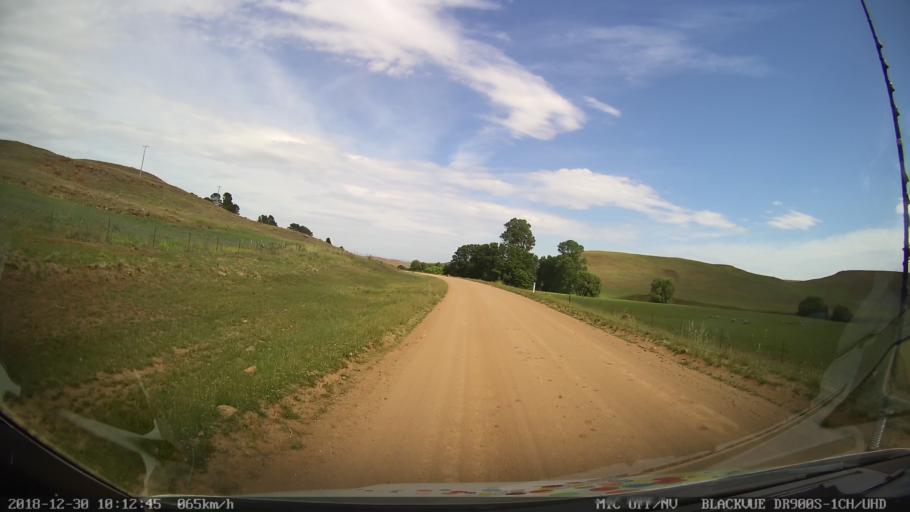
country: AU
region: New South Wales
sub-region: Snowy River
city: Berridale
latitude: -36.5396
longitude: 149.0728
